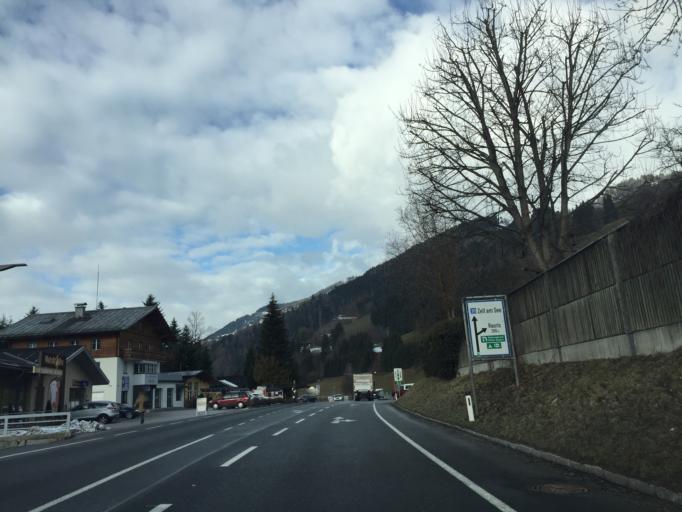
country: AT
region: Salzburg
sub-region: Politischer Bezirk Zell am See
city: Taxenbach
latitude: 47.2920
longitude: 12.9596
